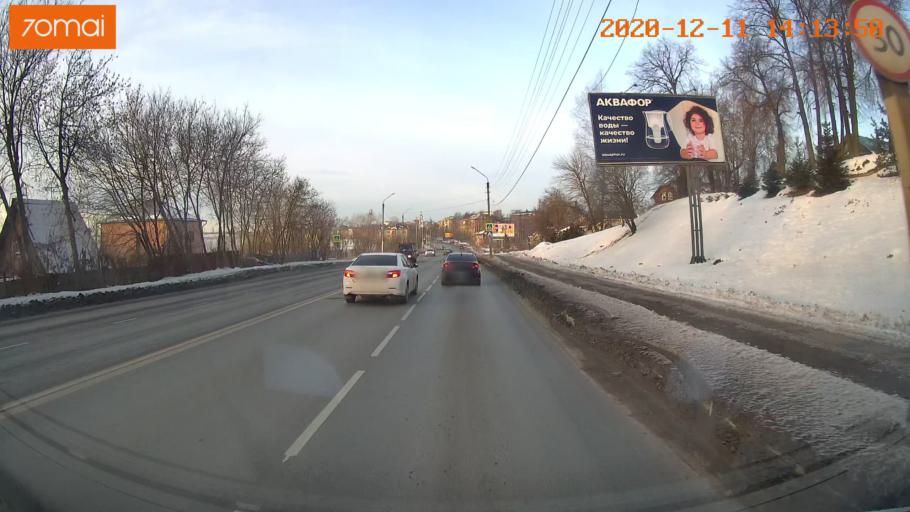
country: RU
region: Kostroma
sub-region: Kostromskoy Rayon
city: Kostroma
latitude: 57.7485
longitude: 40.9557
